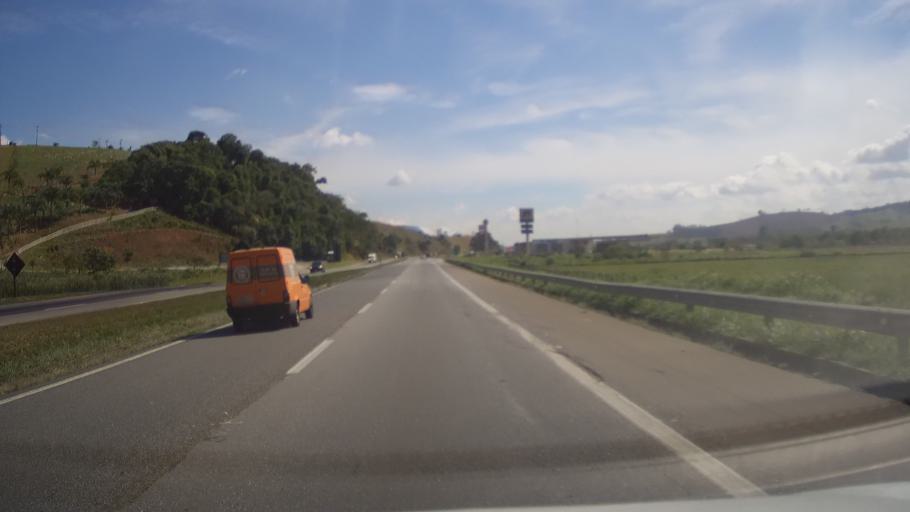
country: BR
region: Minas Gerais
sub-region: Cambui
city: Cambui
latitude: -22.5310
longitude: -46.0277
